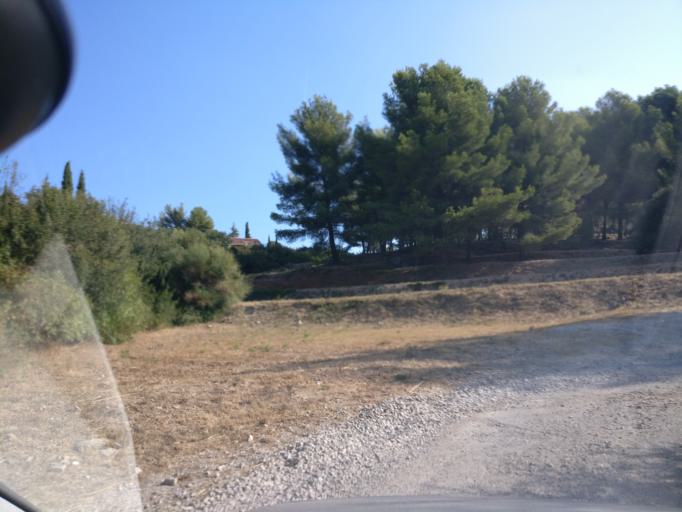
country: FR
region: Provence-Alpes-Cote d'Azur
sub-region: Departement du Var
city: Ollioules
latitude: 43.1375
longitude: 5.8204
